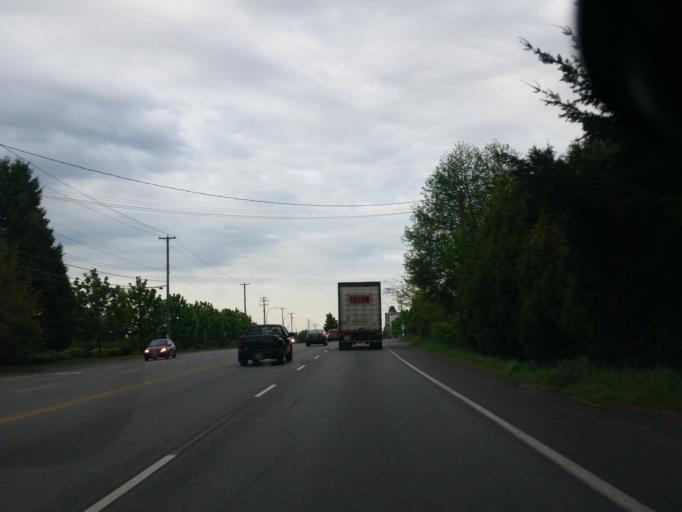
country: CA
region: British Columbia
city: Langley
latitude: 49.1365
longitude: -122.6684
